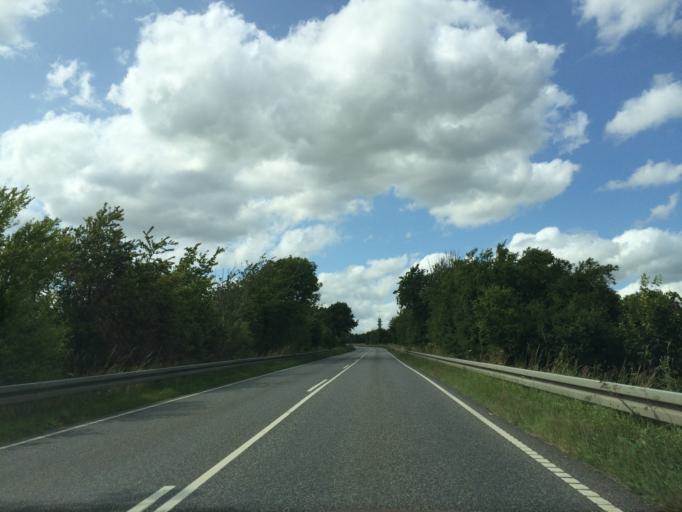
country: DK
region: Central Jutland
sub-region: Skanderborg Kommune
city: Ry
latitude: 56.1713
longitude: 9.8052
